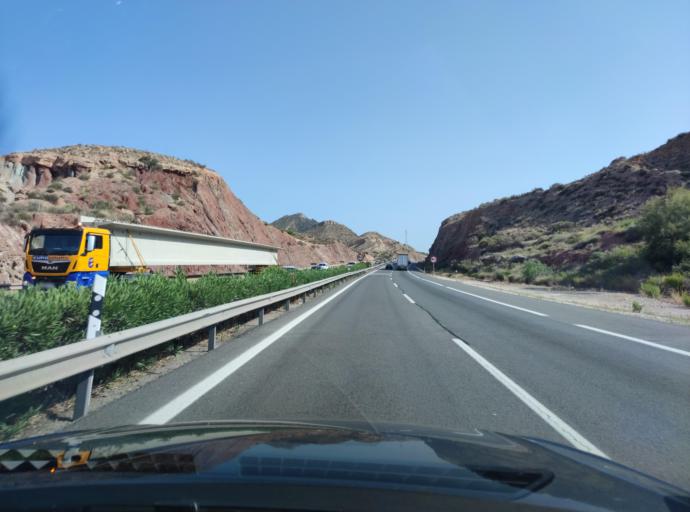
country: ES
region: Valencia
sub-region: Provincia de Alicante
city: Novelda
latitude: 38.4250
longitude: -0.7826
